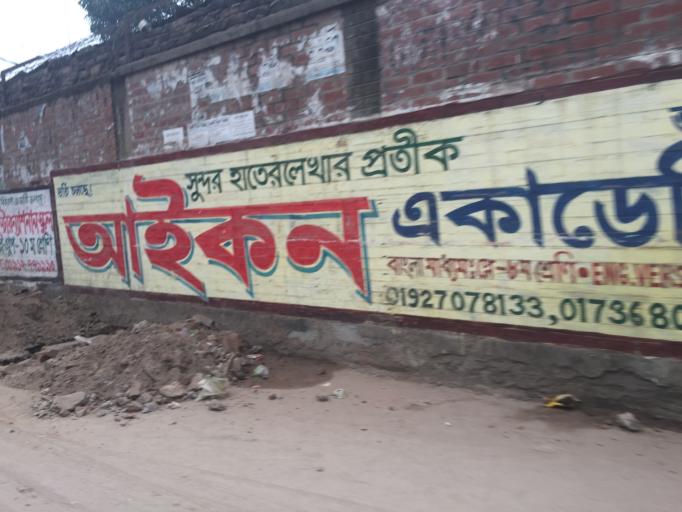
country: BD
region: Dhaka
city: Azimpur
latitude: 23.7863
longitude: 90.3597
